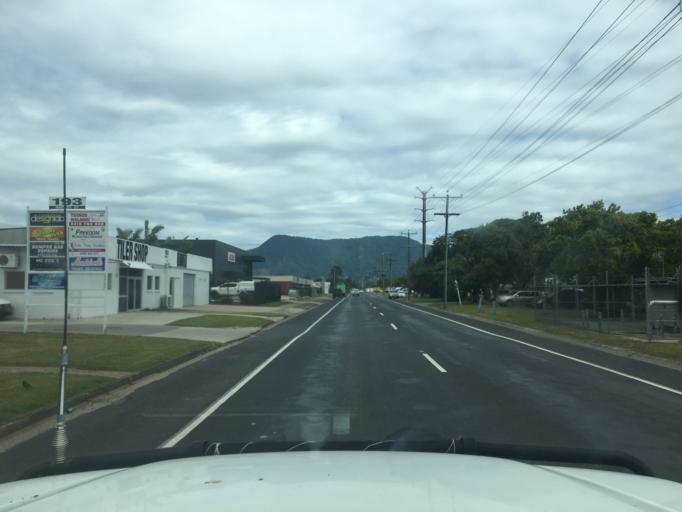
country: AU
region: Queensland
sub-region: Cairns
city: Woree
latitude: -16.9392
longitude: 145.7622
